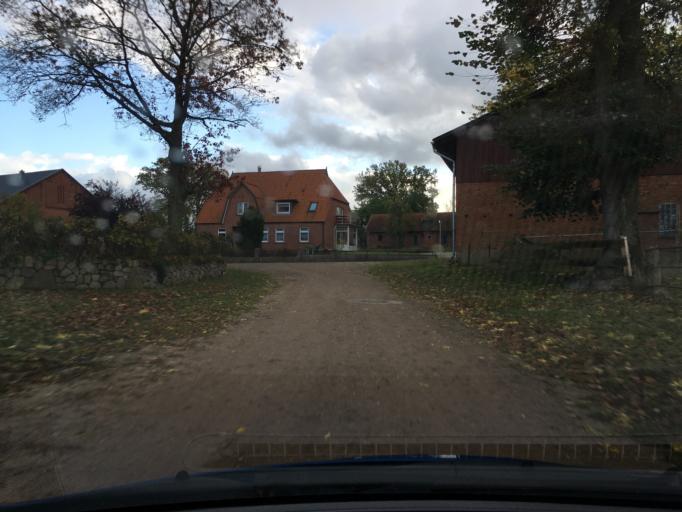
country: DE
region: Lower Saxony
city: Reinstorf
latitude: 53.2509
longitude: 10.5656
